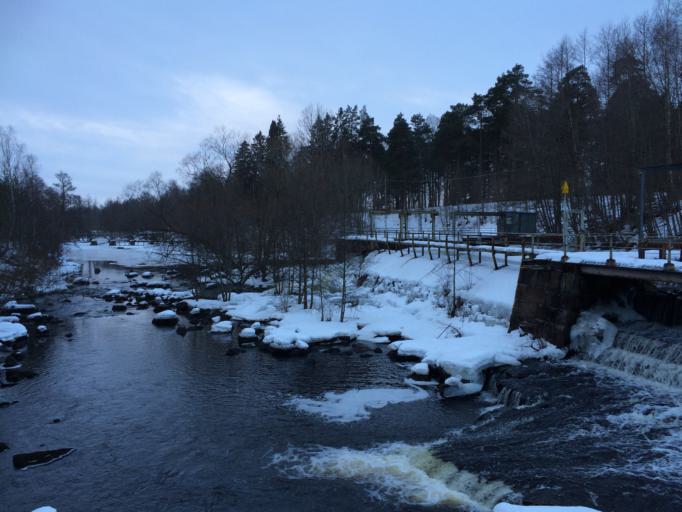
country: SE
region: Vaestmanland
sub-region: Hallstahammars Kommun
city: Hallstahammar
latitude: 59.6231
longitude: 16.2070
